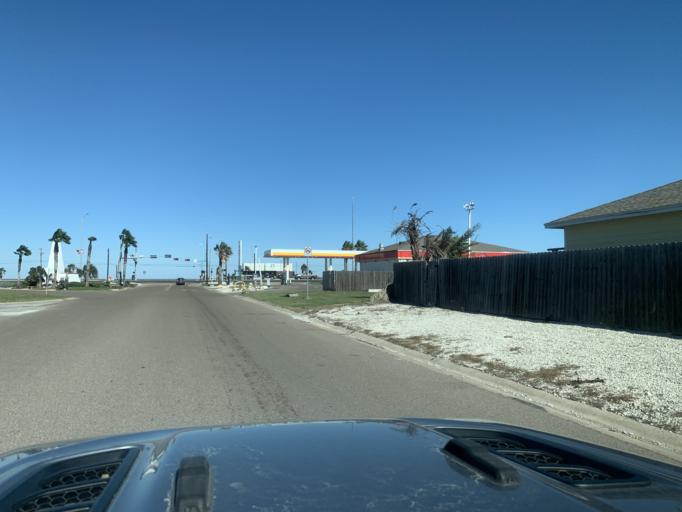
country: US
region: Texas
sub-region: Nueces County
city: Corpus Christi
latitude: 27.6278
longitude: -97.2266
